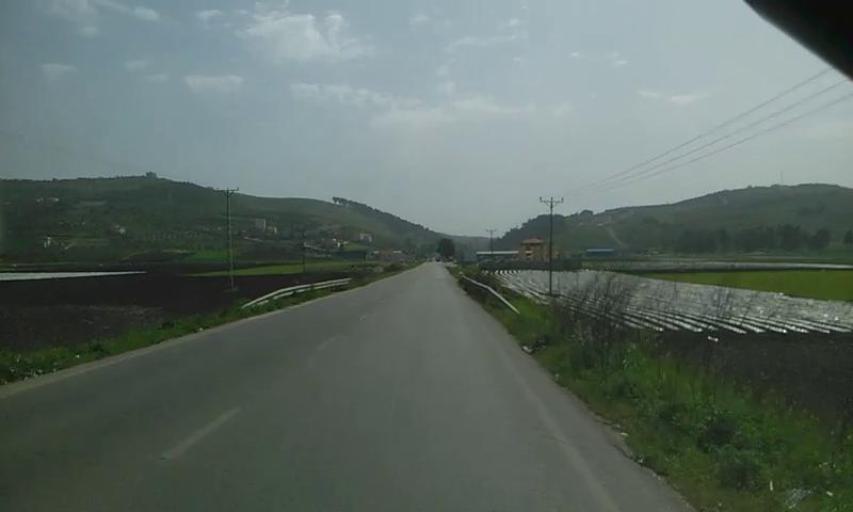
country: PS
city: Bir al Basha
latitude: 32.4138
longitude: 35.2286
